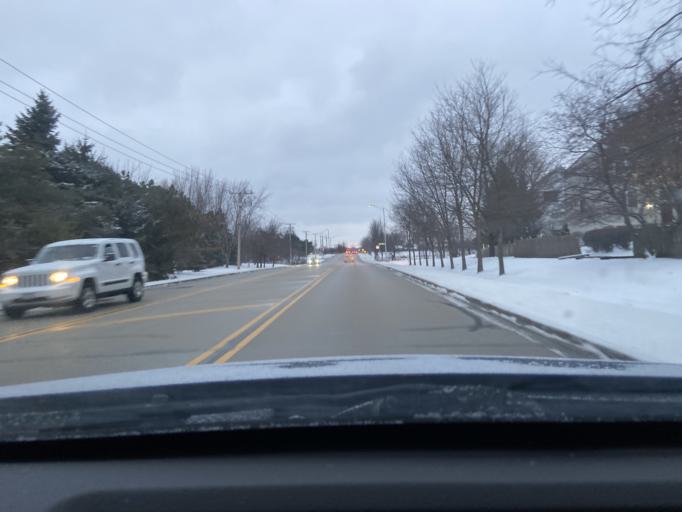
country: US
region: Illinois
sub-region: Lake County
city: Third Lake
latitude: 42.3573
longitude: -88.0241
